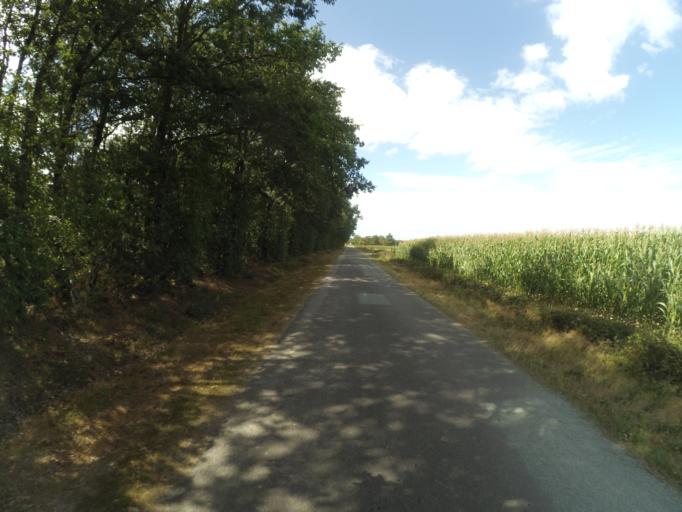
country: FR
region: Pays de la Loire
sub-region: Departement de la Loire-Atlantique
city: Remouille
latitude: 47.0407
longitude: -1.4069
